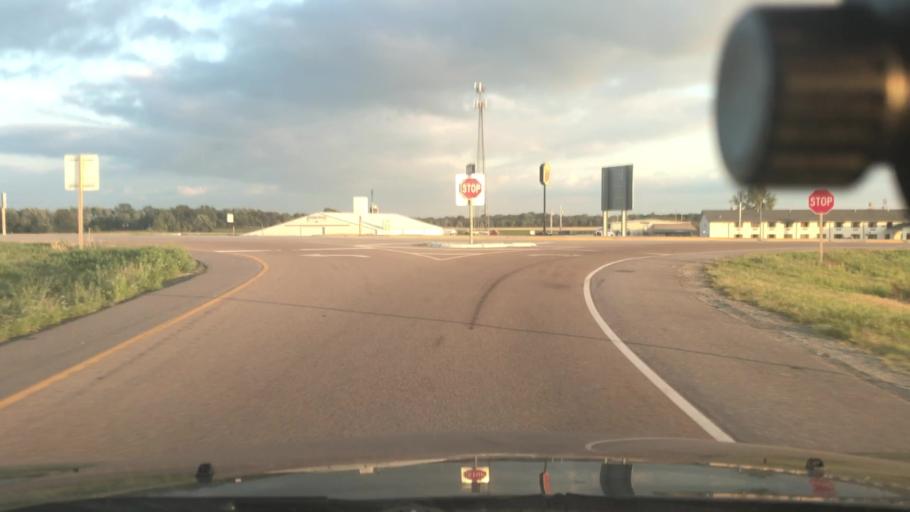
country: US
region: Illinois
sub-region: Washington County
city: Okawville
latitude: 38.4388
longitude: -89.5328
